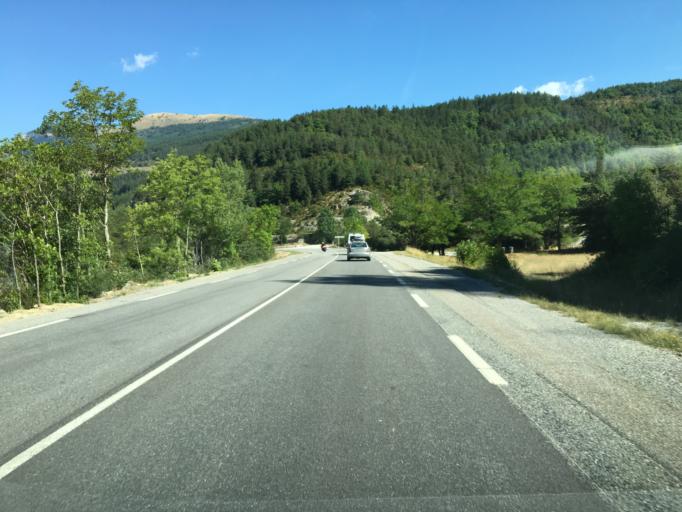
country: FR
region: Provence-Alpes-Cote d'Azur
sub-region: Departement des Hautes-Alpes
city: Veynes
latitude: 44.5544
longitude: 5.7670
